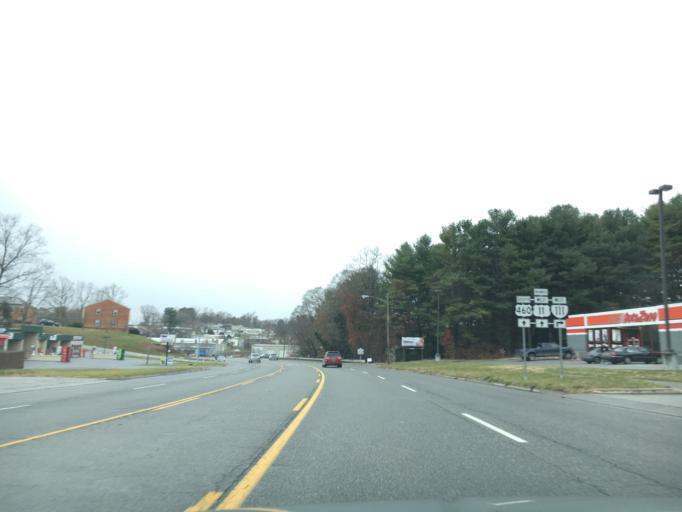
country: US
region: Virginia
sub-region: Montgomery County
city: Christiansburg
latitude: 37.1345
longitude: -80.3870
